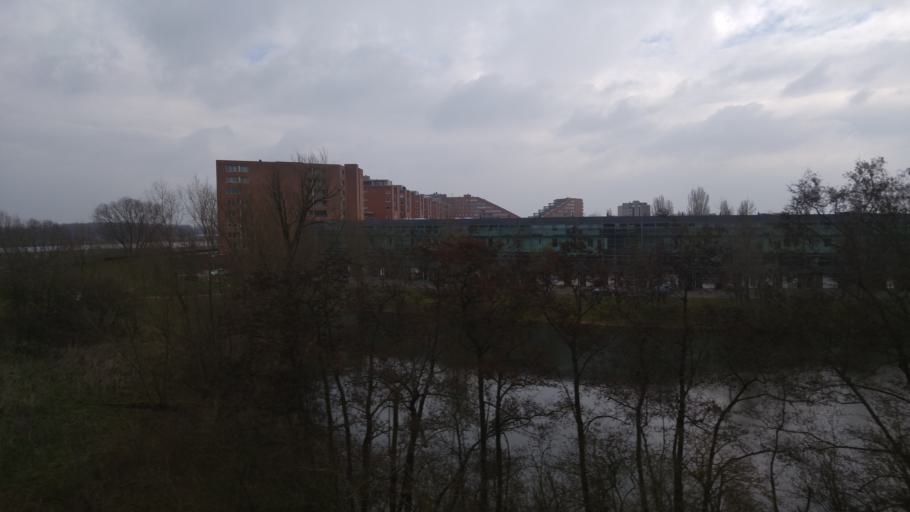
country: NL
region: Gelderland
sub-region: Gemeente Maasdriel
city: Hedel
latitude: 51.7370
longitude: 5.2749
